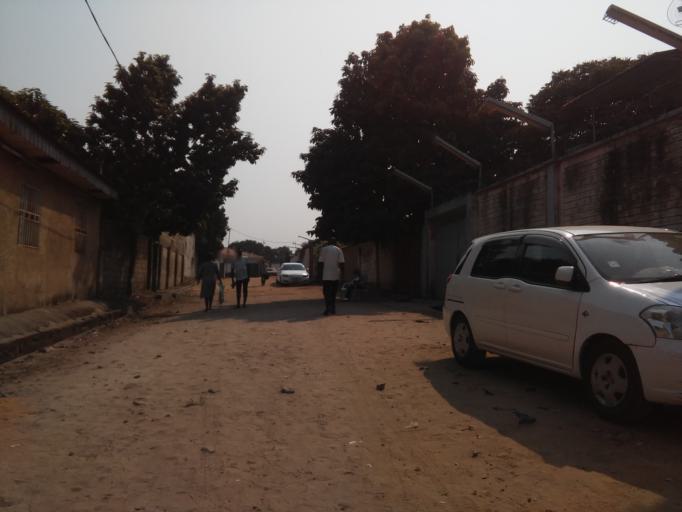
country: CD
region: Kinshasa
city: Kinshasa
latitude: -4.3445
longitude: 15.2642
